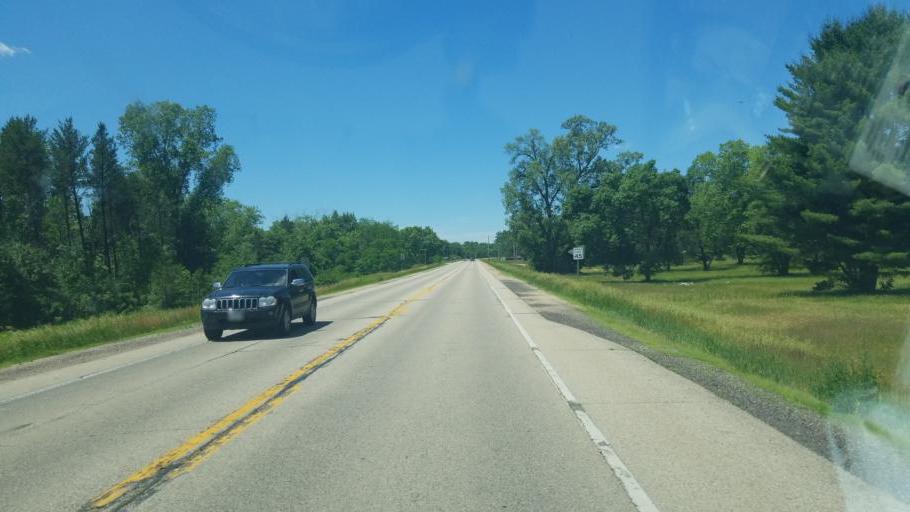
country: US
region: Wisconsin
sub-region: Juneau County
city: New Lisbon
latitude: 44.0280
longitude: -90.0576
